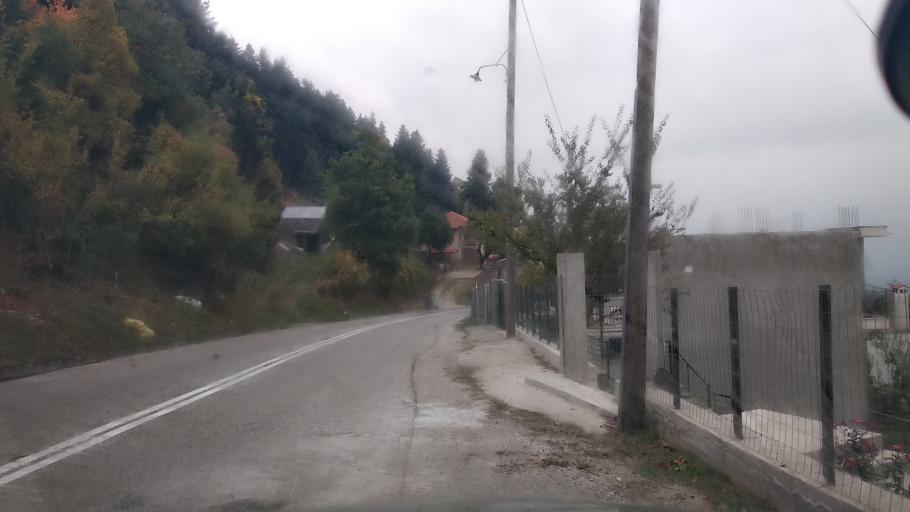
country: GR
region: Thessaly
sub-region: Trikala
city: Pyli
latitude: 39.5063
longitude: 21.5346
